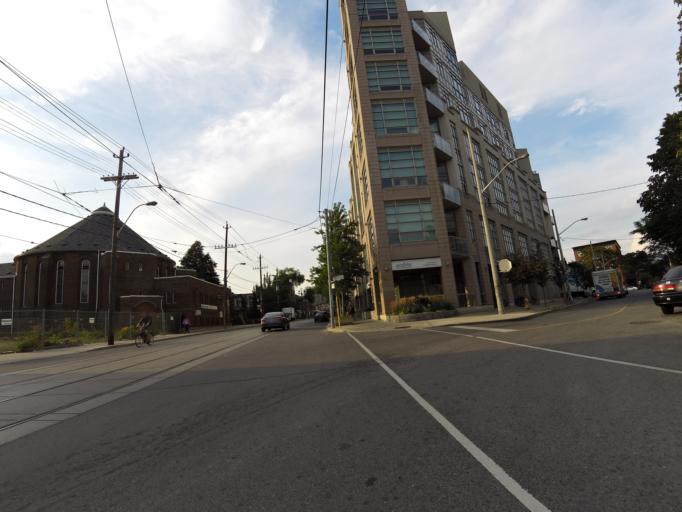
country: CA
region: Ontario
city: Toronto
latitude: 43.6518
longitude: -79.4511
